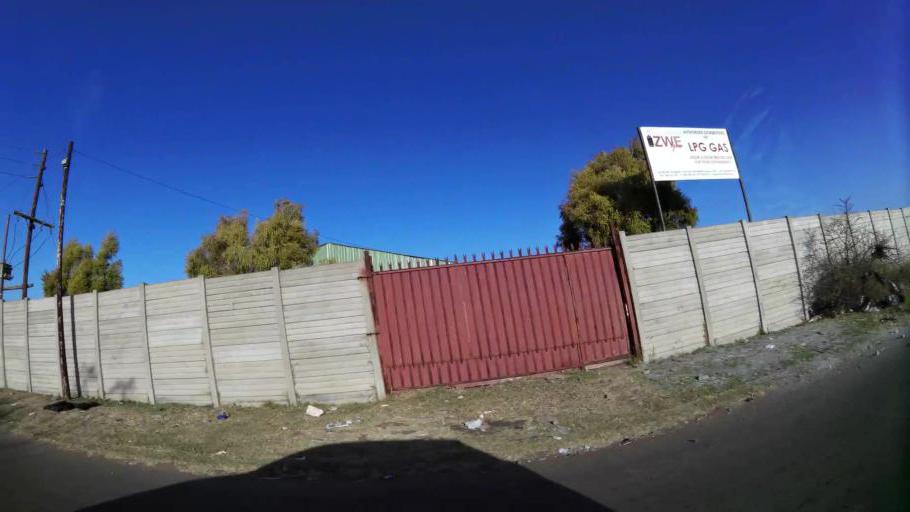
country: ZA
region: North-West
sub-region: Bojanala Platinum District Municipality
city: Rustenburg
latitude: -25.6342
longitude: 27.2211
